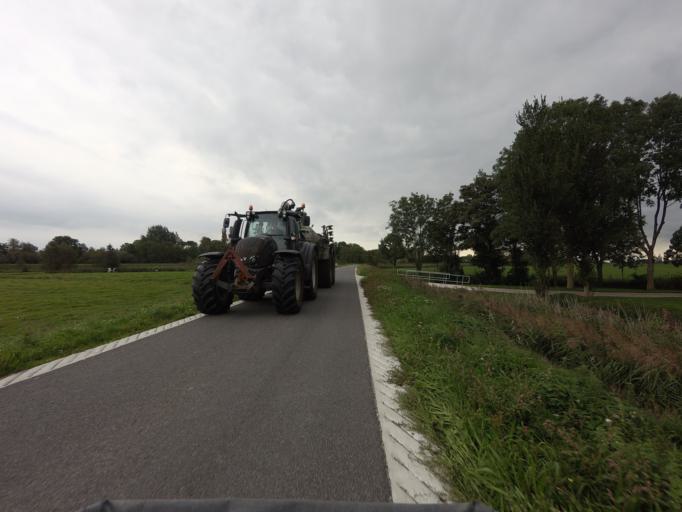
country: NL
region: Friesland
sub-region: Sudwest Fryslan
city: IJlst
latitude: 53.0173
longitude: 5.6177
